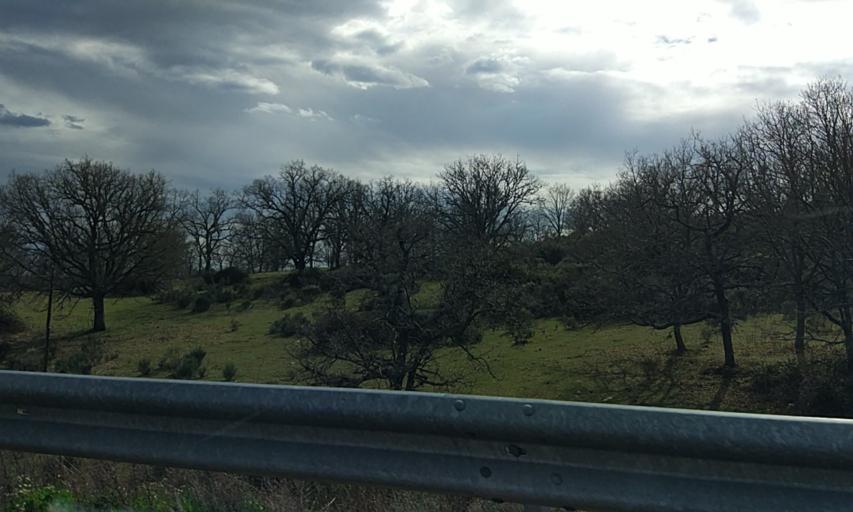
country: ES
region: Castille and Leon
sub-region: Provincia de Salamanca
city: Robleda
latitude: 40.4323
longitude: -6.6049
